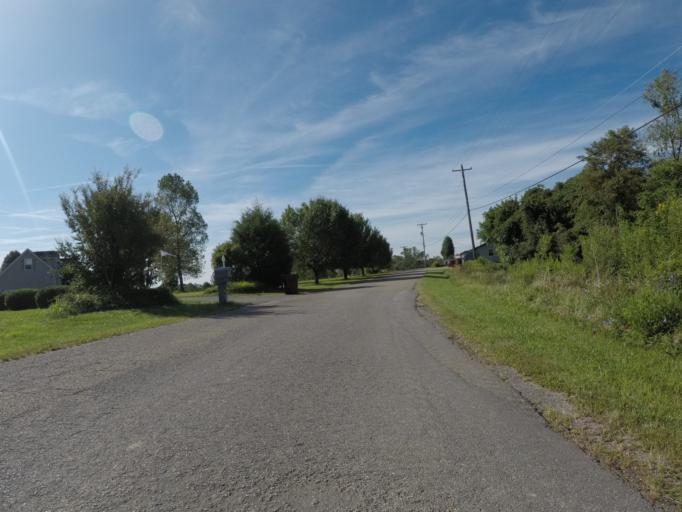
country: US
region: West Virginia
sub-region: Cabell County
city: Huntington
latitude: 38.4625
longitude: -82.4609
